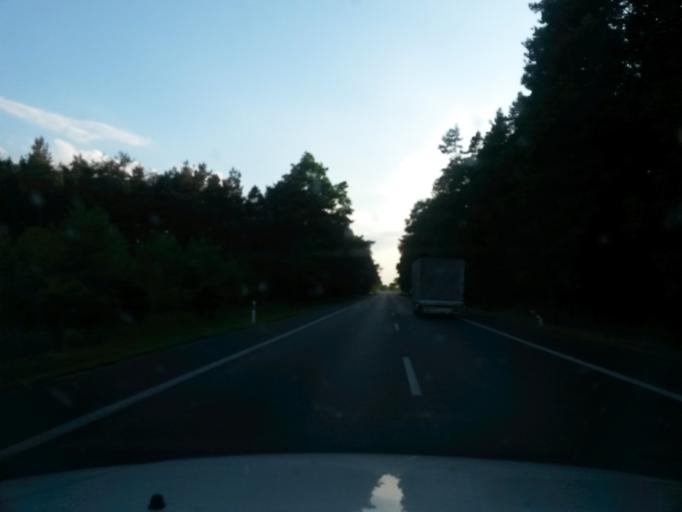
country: PL
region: Lodz Voivodeship
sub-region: Powiat wielunski
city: Wierzchlas
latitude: 51.2499
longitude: 18.7071
